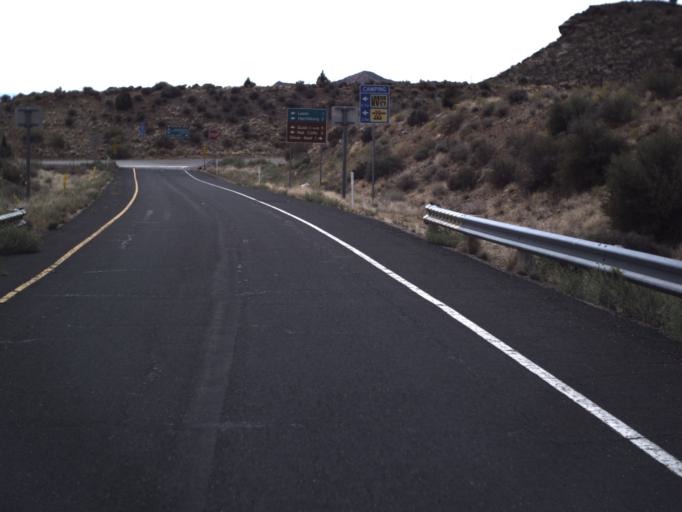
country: US
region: Utah
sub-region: Washington County
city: Toquerville
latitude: 37.2451
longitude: -113.3523
